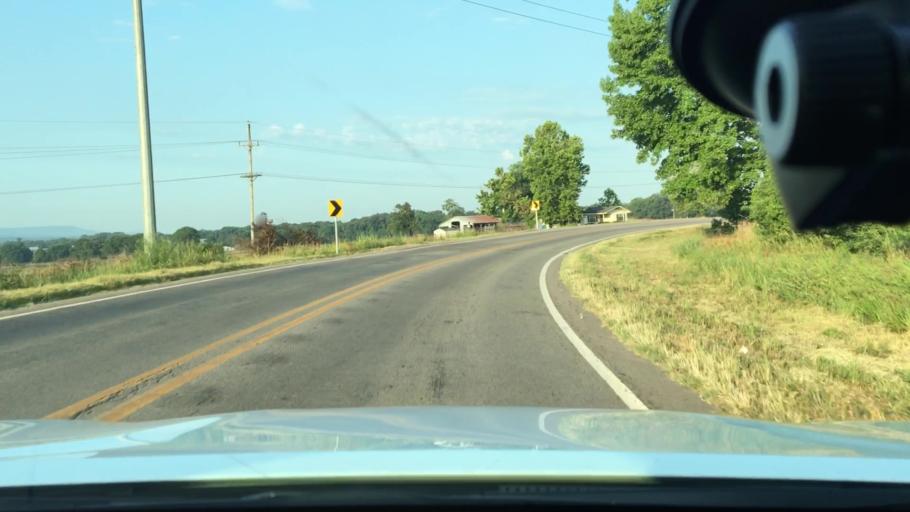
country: US
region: Arkansas
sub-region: Johnson County
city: Coal Hill
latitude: 35.3749
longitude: -93.5620
